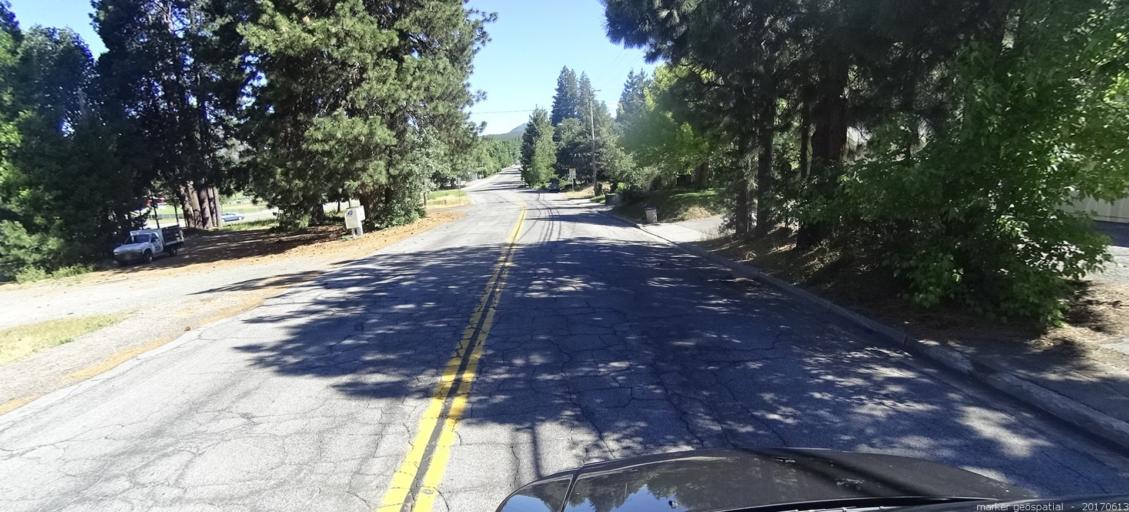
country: US
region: California
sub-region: Siskiyou County
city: Mount Shasta
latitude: 41.3165
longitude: -122.3062
